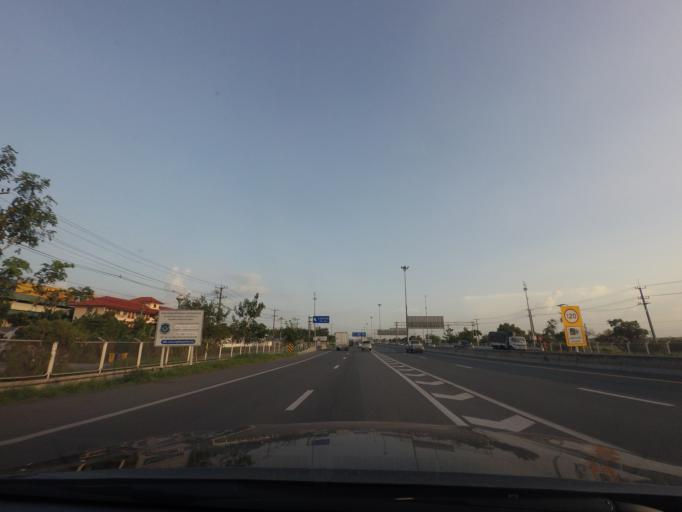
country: TH
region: Phra Nakhon Si Ayutthaya
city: Bang Pa-in
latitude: 14.1822
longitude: 100.6408
